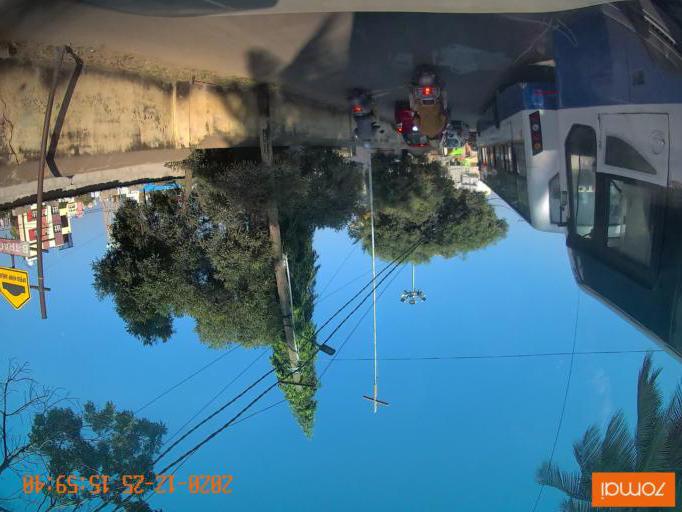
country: IN
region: Karnataka
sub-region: Bangalore Urban
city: Bangalore
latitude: 12.8739
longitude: 77.6259
